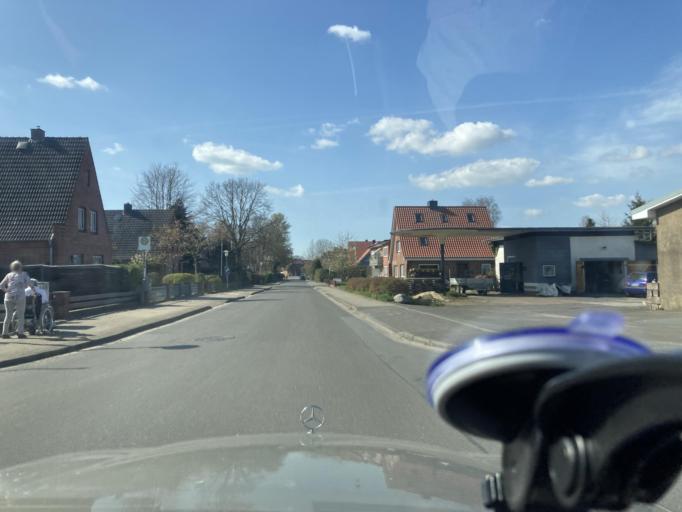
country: DE
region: Schleswig-Holstein
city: Friedrichstadt
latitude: 54.3741
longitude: 9.0945
